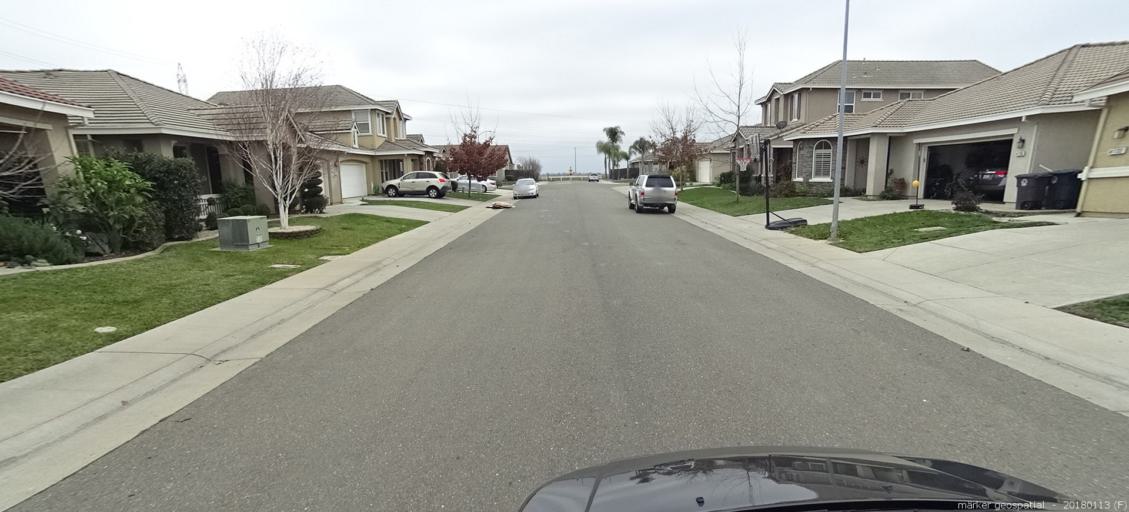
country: US
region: California
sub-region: Sacramento County
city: Gold River
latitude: 38.5529
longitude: -121.2124
